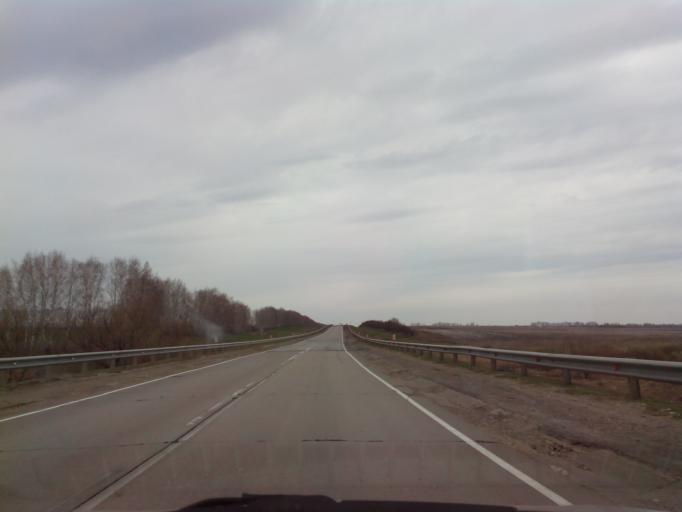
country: RU
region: Tambov
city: Znamenka
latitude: 52.4197
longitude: 41.3764
